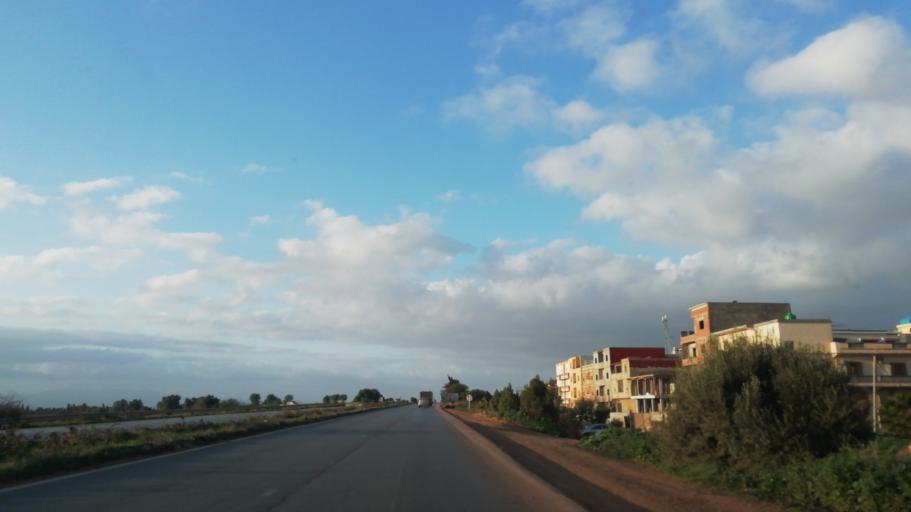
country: DZ
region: Oran
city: Es Senia
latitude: 35.6140
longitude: -0.7223
